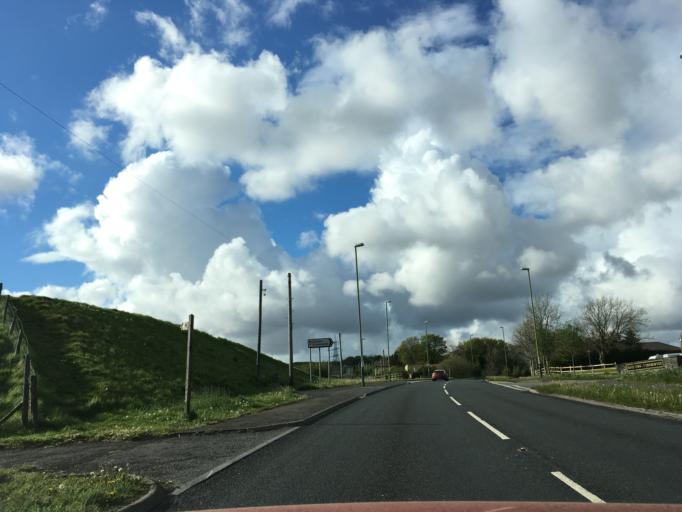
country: GB
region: Wales
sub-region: Caerphilly County Borough
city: Rhymney
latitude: 51.7732
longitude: -3.3006
